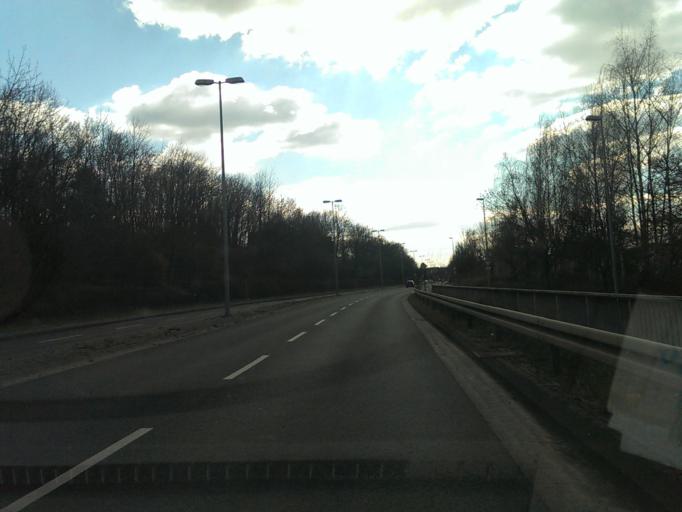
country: DE
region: Lower Saxony
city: Hildesheim
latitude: 52.1490
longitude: 9.9653
